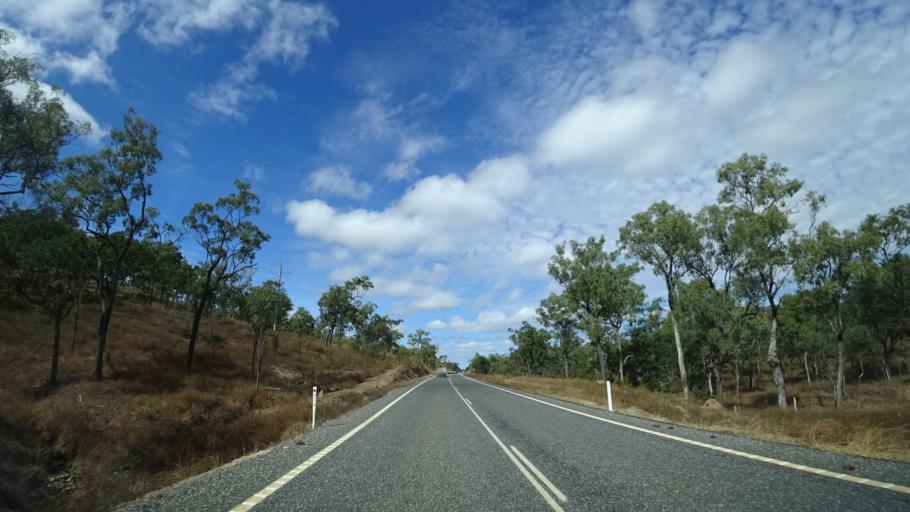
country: AU
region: Queensland
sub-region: Cairns
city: Port Douglas
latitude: -16.3076
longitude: 144.7171
